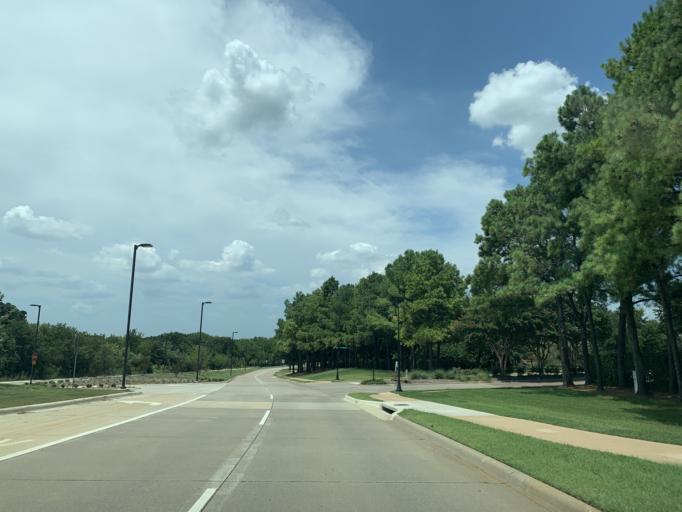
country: US
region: Texas
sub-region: Denton County
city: Trophy Club
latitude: 32.9737
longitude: -97.1550
